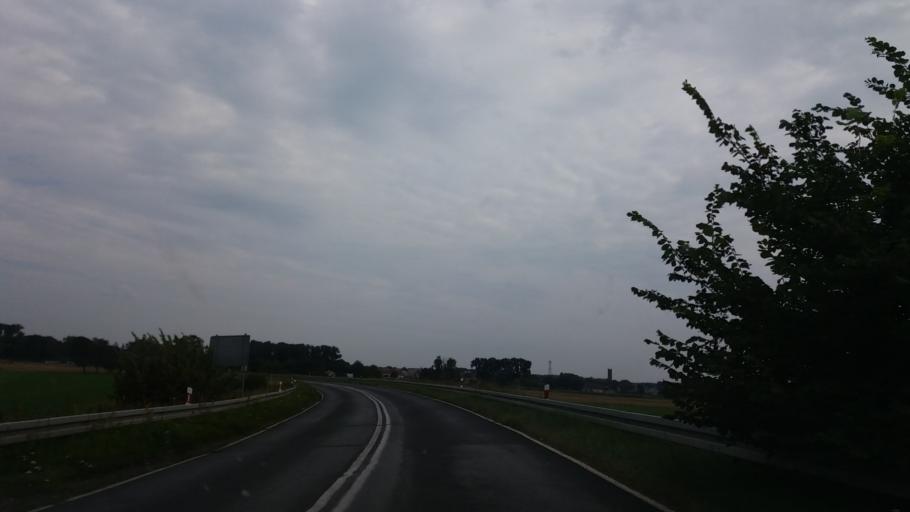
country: PL
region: Lubusz
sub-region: Powiat miedzyrzecki
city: Skwierzyna
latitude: 52.6047
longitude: 15.4867
